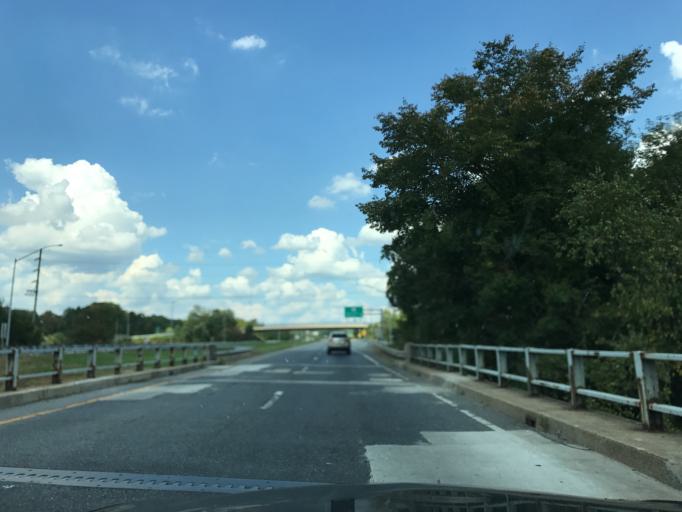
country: US
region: Maryland
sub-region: Queen Anne's County
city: Kingstown
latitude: 39.2611
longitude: -75.8641
